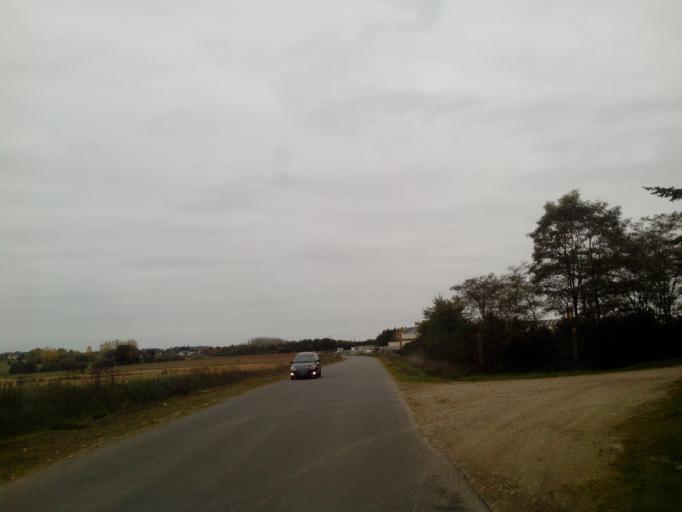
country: FR
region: Brittany
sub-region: Departement du Morbihan
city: Mauron
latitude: 48.0691
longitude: -2.3036
